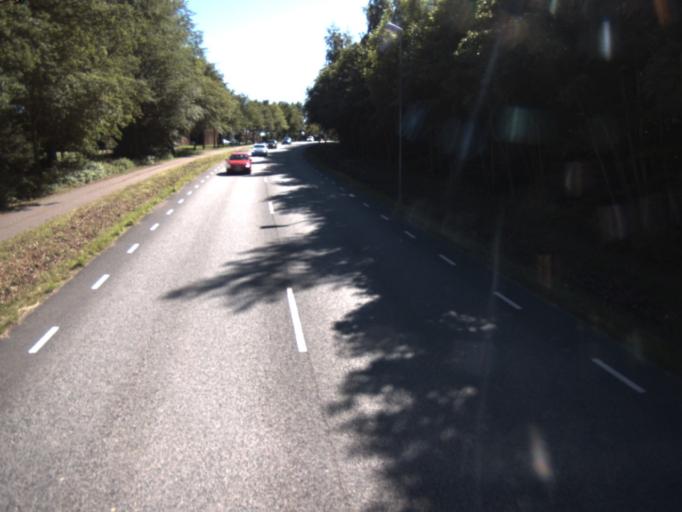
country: SE
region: Skane
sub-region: Helsingborg
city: Odakra
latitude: 56.0871
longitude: 12.7429
